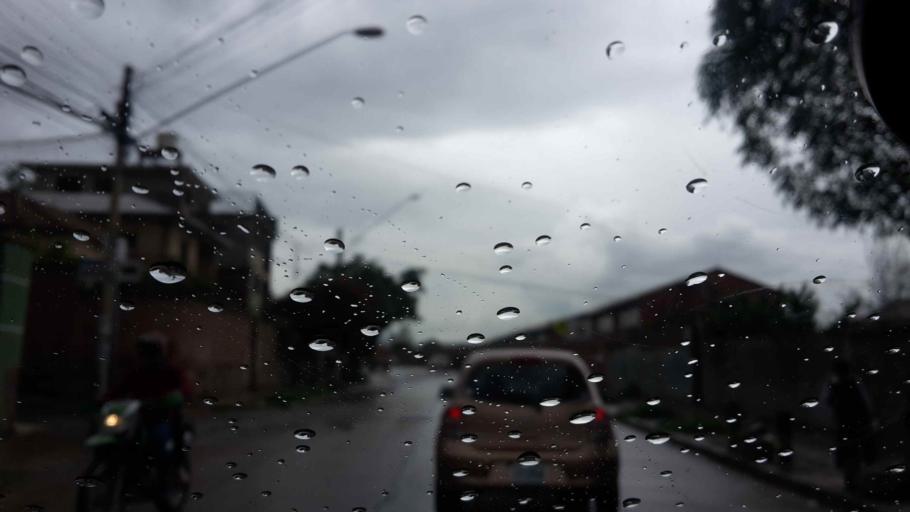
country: BO
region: Cochabamba
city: Cochabamba
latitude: -17.4143
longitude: -66.1495
